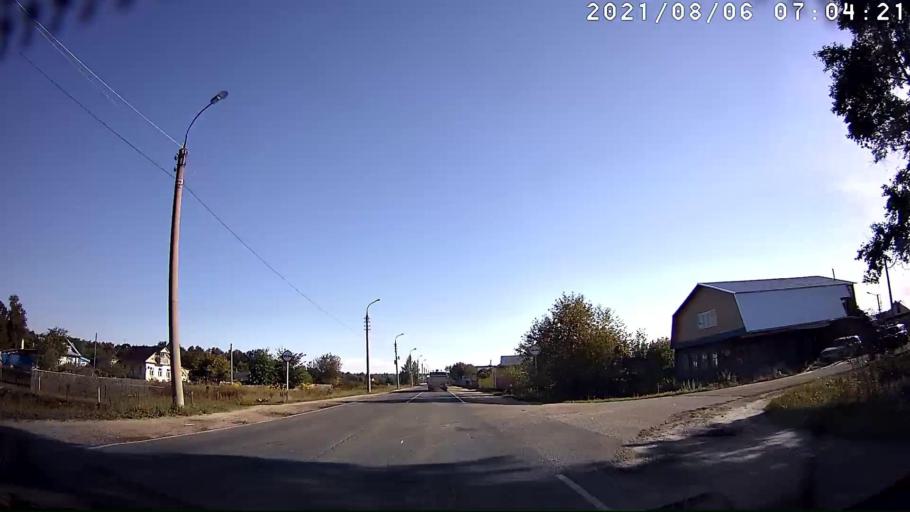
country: RU
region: Mariy-El
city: Yoshkar-Ola
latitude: 56.5464
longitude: 47.9819
